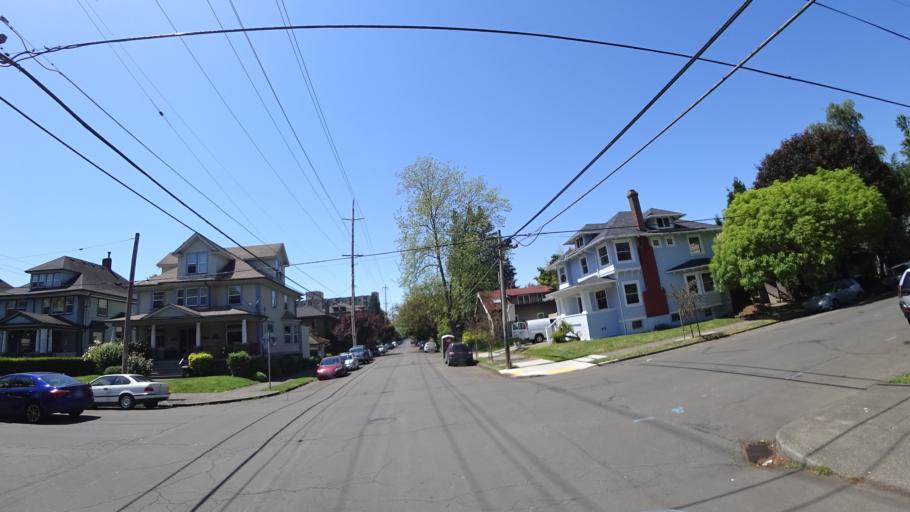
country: US
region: Oregon
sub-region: Multnomah County
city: Portland
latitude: 45.5365
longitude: -122.6534
